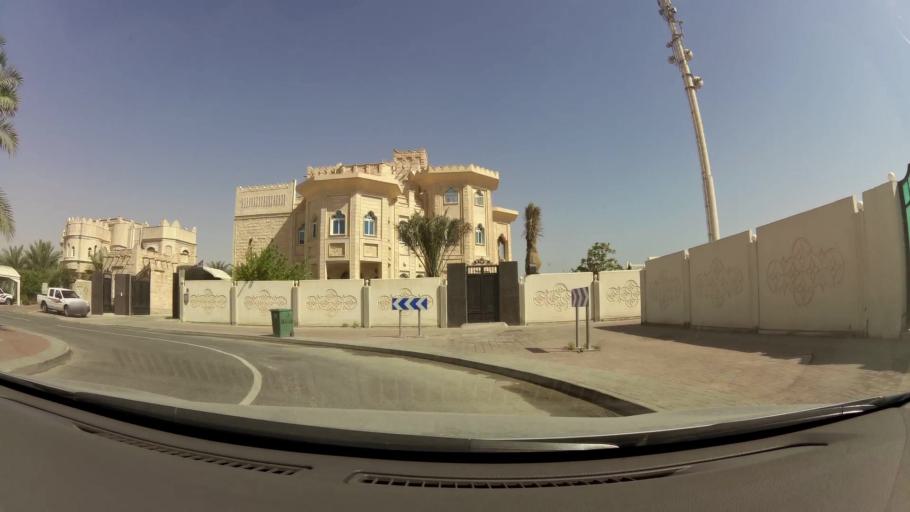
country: QA
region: Baladiyat ad Dawhah
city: Doha
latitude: 25.3557
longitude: 51.5102
